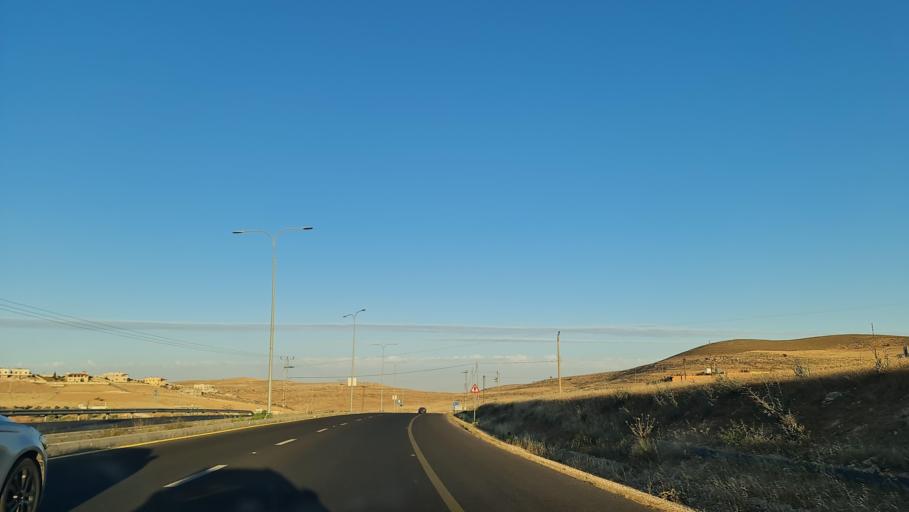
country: JO
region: Zarqa
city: Russeifa
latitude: 32.0869
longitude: 35.9990
